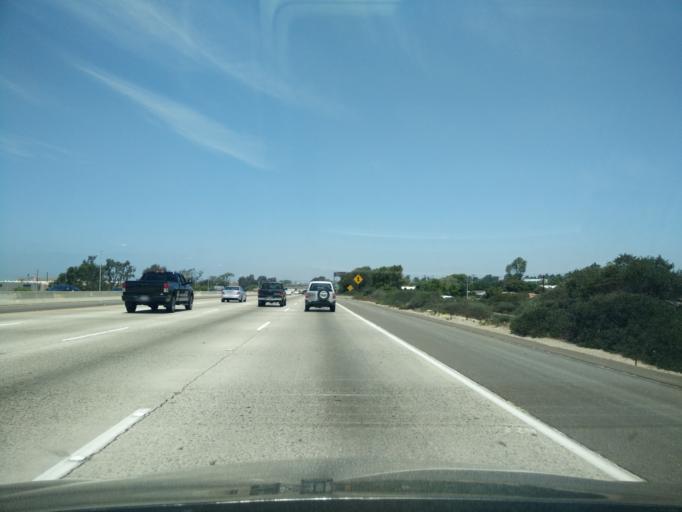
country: US
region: California
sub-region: San Diego County
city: Chula Vista
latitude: 32.6231
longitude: -117.0934
